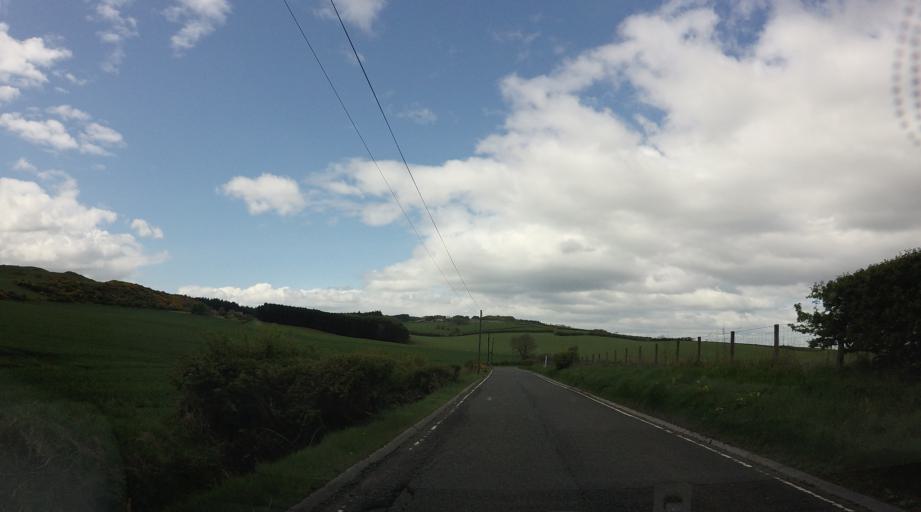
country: GB
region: Scotland
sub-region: West Lothian
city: Linlithgow
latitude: 55.9548
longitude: -3.5662
